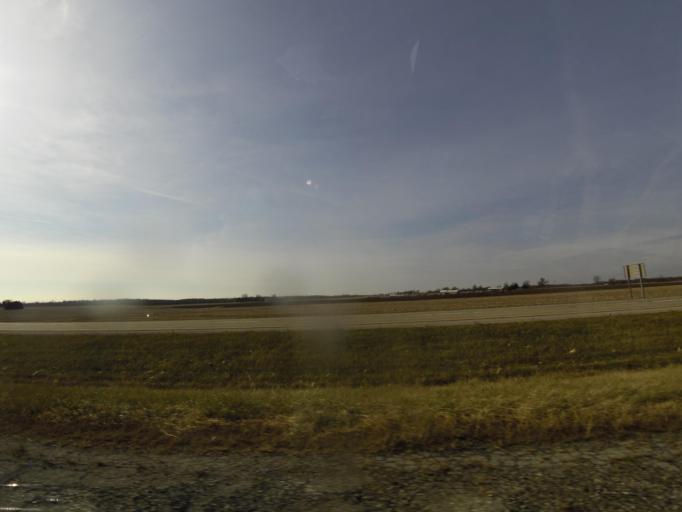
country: US
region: Illinois
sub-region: De Witt County
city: Clinton
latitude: 40.1439
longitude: -88.9824
